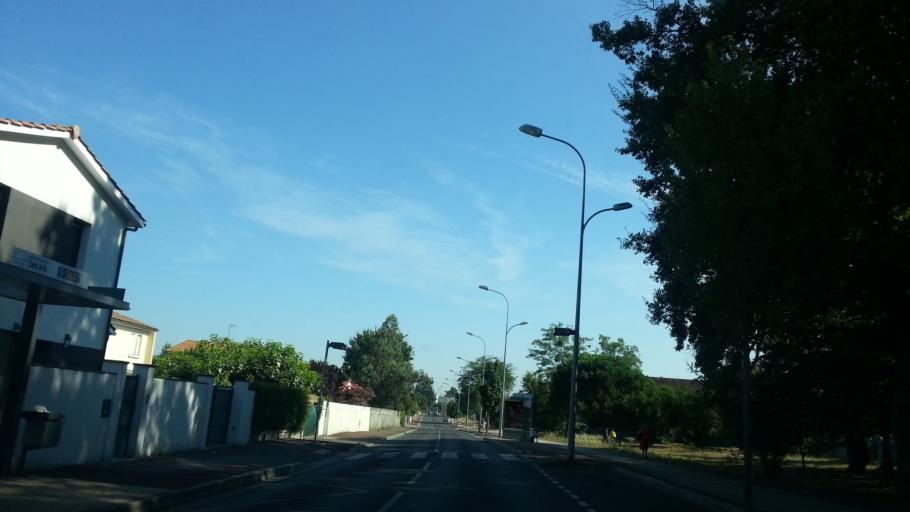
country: FR
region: Aquitaine
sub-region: Departement de la Gironde
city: Leognan
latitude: 44.7587
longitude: -0.5829
